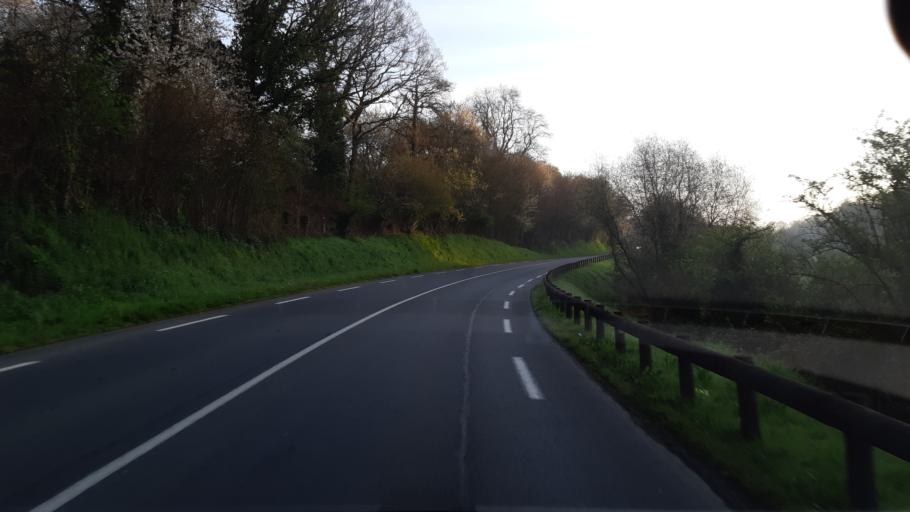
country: FR
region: Lower Normandy
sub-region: Departement de la Manche
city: Agneaux
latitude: 49.0743
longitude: -1.1273
